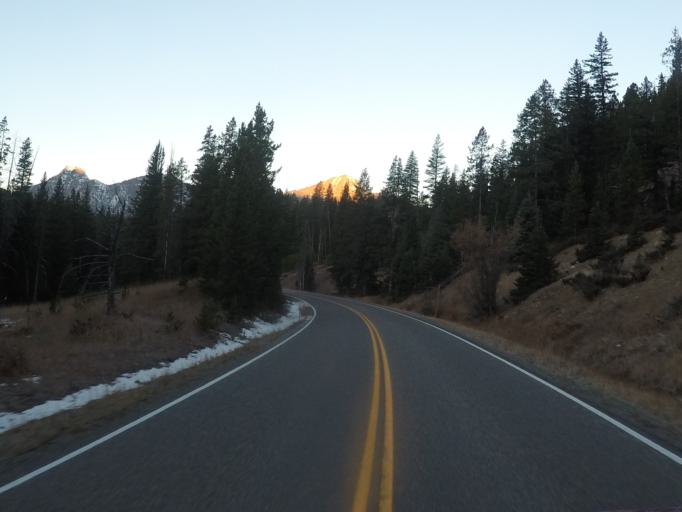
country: US
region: Montana
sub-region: Stillwater County
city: Absarokee
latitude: 45.0053
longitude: -110.0184
